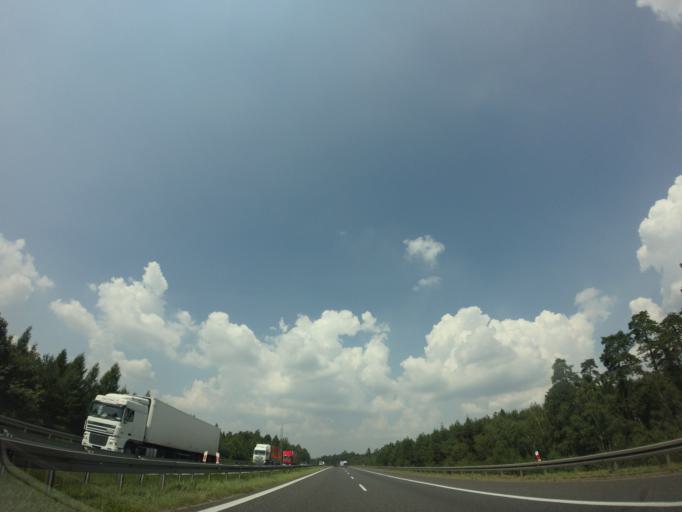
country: PL
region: Silesian Voivodeship
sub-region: Powiat gliwicki
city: Sosnicowice
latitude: 50.3578
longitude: 18.5194
